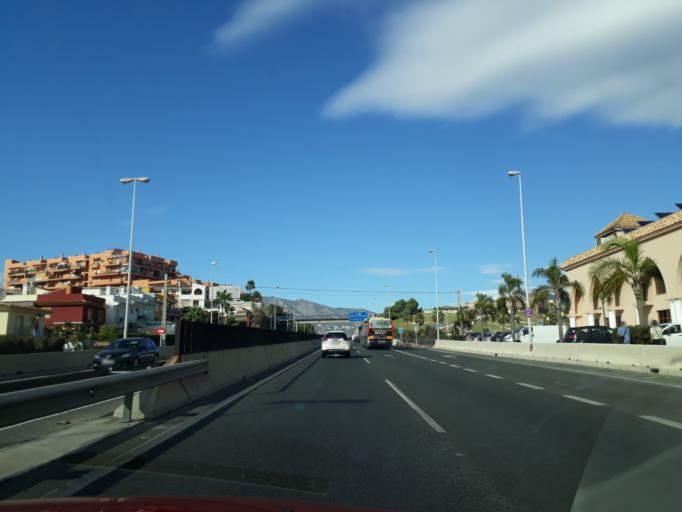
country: ES
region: Andalusia
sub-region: Provincia de Malaga
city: Fuengirola
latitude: 36.5217
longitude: -4.6301
